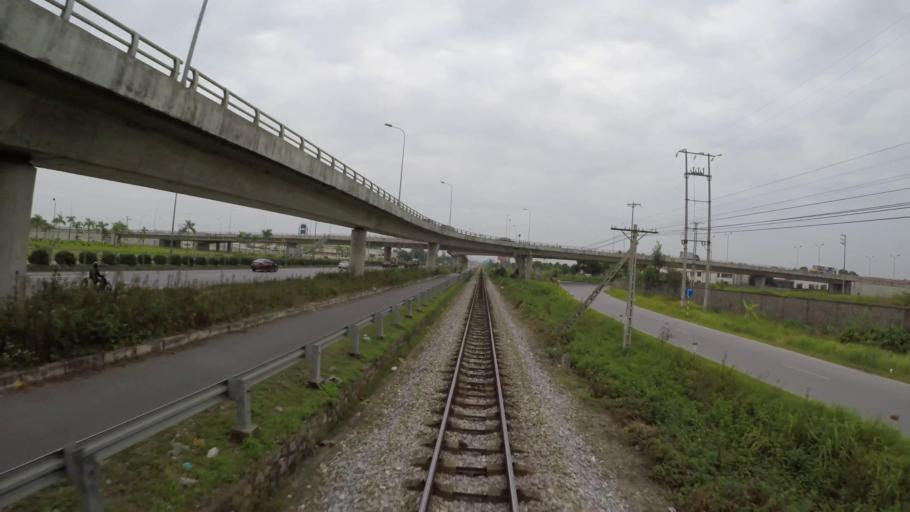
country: VN
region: Hai Duong
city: Nam Sach
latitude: 20.9643
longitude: 106.3749
